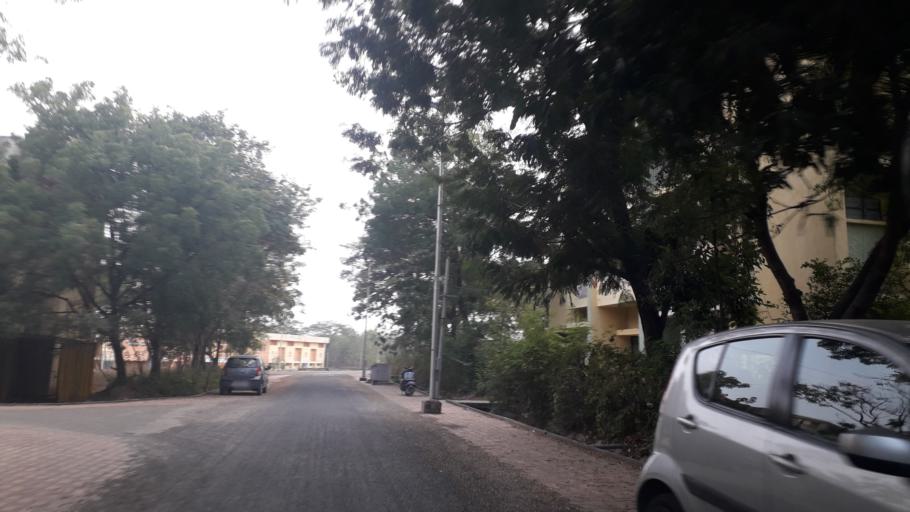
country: IN
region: Telangana
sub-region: Rangareddi
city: Singapur
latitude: 17.4664
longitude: 78.1648
